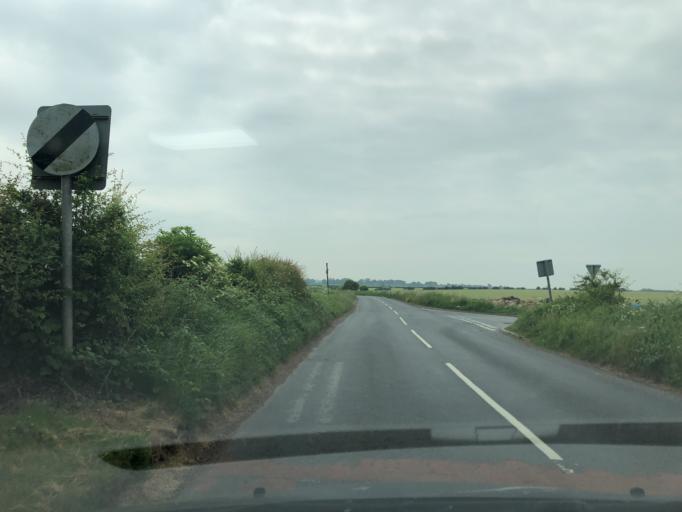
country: GB
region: England
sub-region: North Yorkshire
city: Boroughbridge
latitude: 54.1290
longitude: -1.4036
